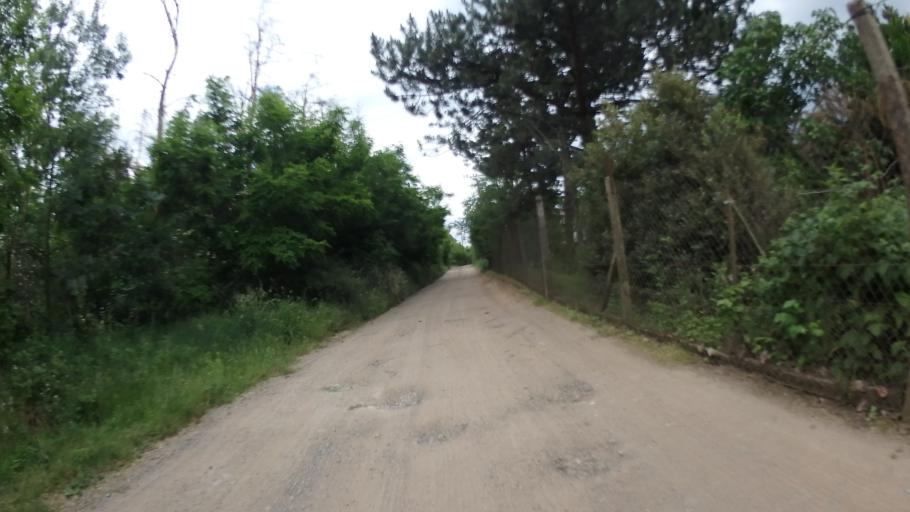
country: CZ
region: South Moravian
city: Ostopovice
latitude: 49.1383
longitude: 16.5433
